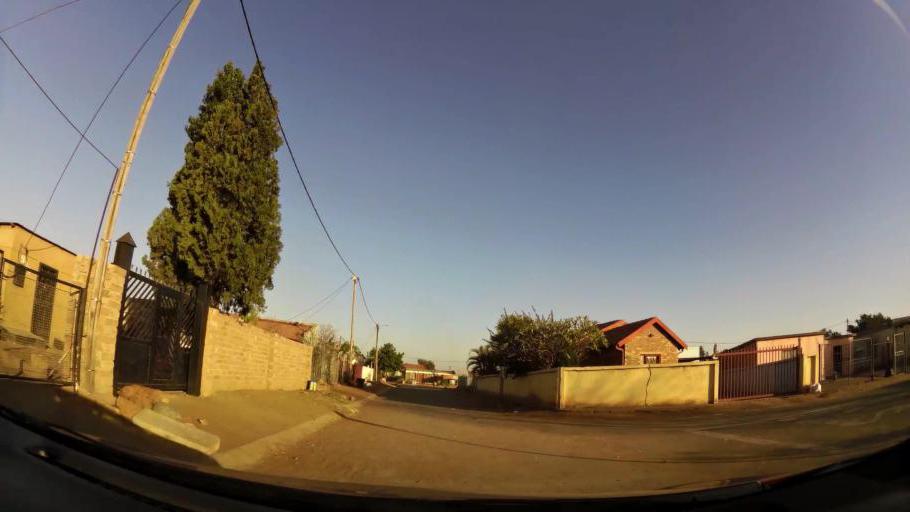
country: ZA
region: Gauteng
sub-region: City of Tshwane Metropolitan Municipality
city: Mabopane
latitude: -25.6032
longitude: 28.1066
